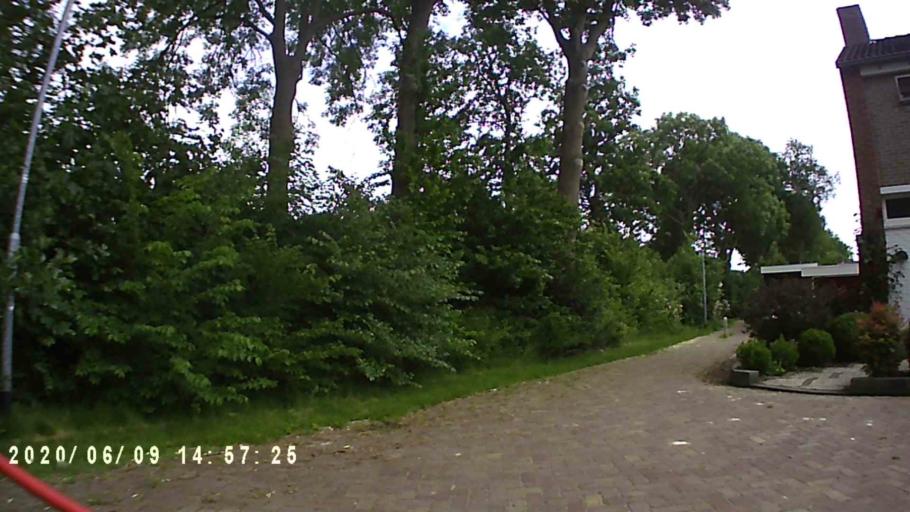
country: NL
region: Groningen
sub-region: Gemeente Winsum
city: Winsum
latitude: 53.3268
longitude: 6.5210
